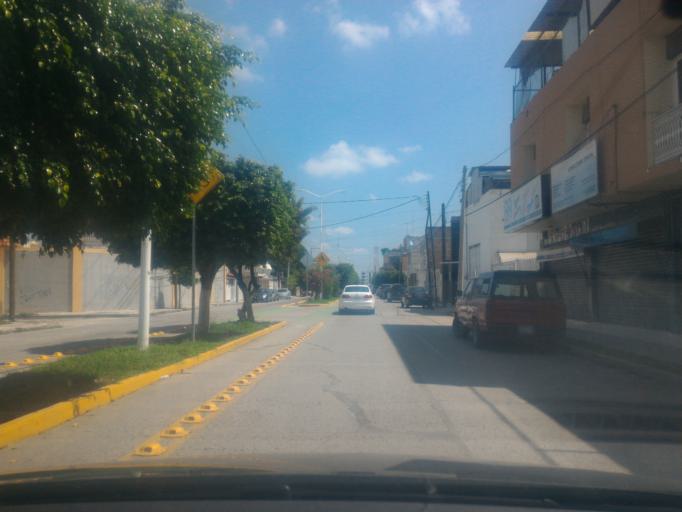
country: MX
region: Guanajuato
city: San Francisco del Rincon
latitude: 21.0111
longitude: -101.8586
